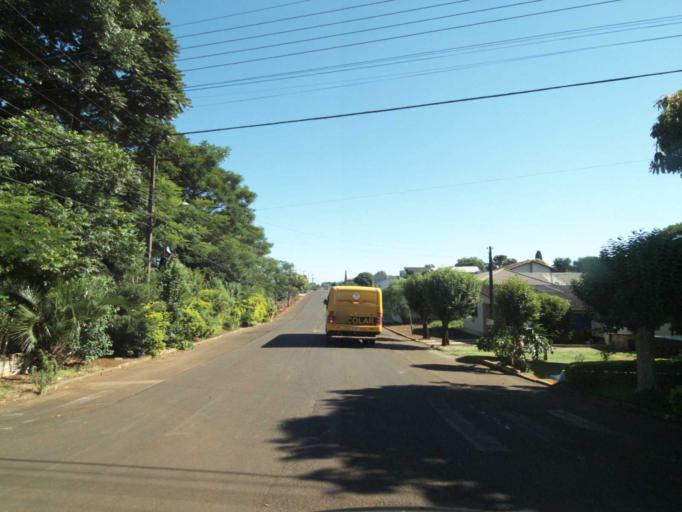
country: BR
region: Parana
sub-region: Coronel Vivida
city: Coronel Vivida
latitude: -25.9623
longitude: -52.8187
